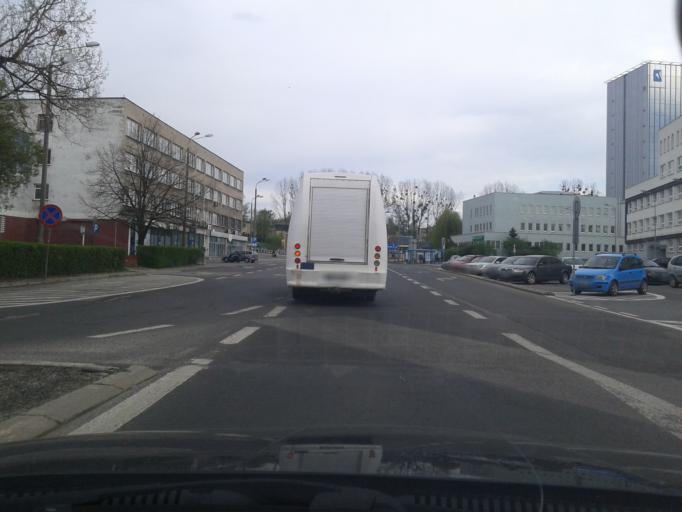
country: PL
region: Silesian Voivodeship
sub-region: Rybnik
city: Rybnik
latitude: 50.0889
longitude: 18.5416
